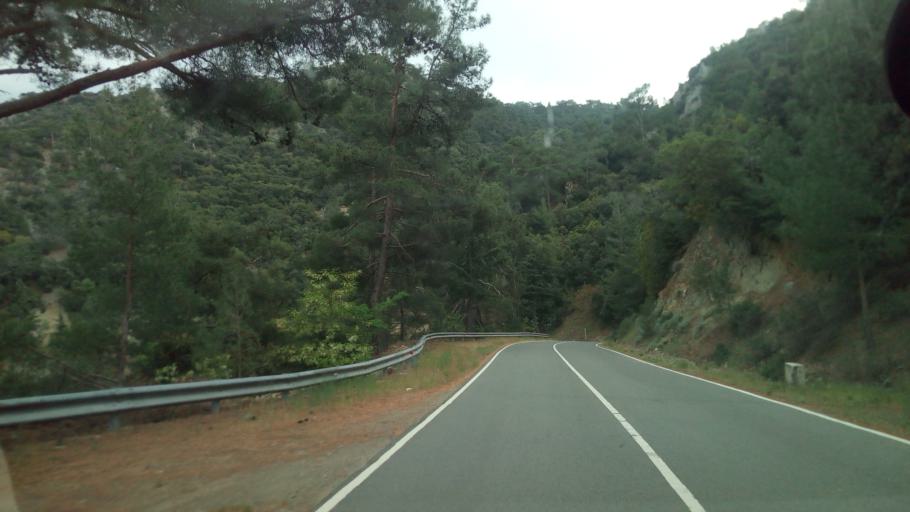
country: CY
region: Lefkosia
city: Kato Pyrgos
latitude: 35.0118
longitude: 32.6733
